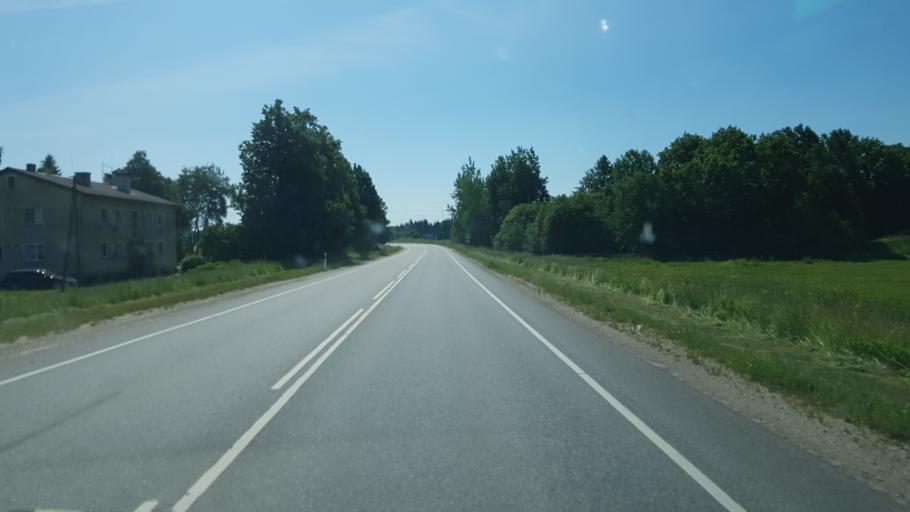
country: EE
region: Tartu
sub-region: Tartu linn
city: Tartu
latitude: 58.3640
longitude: 26.8884
